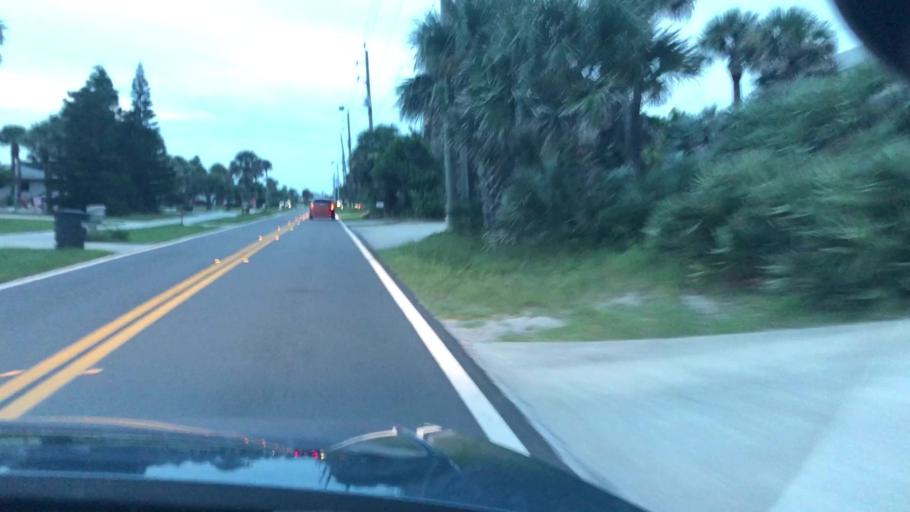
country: US
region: Florida
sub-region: Volusia County
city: Ponce Inlet
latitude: 29.1193
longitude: -80.9507
